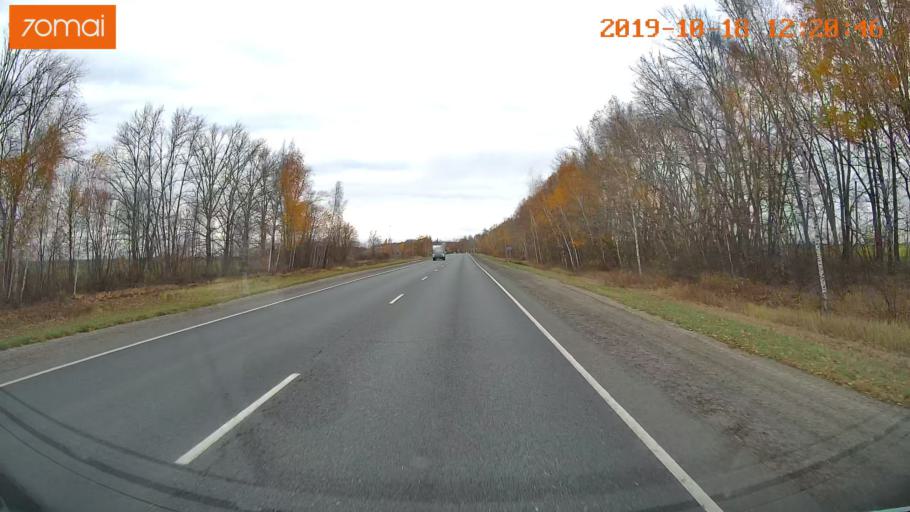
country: RU
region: Rjazan
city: Bagramovo
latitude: 54.5029
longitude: 39.4843
